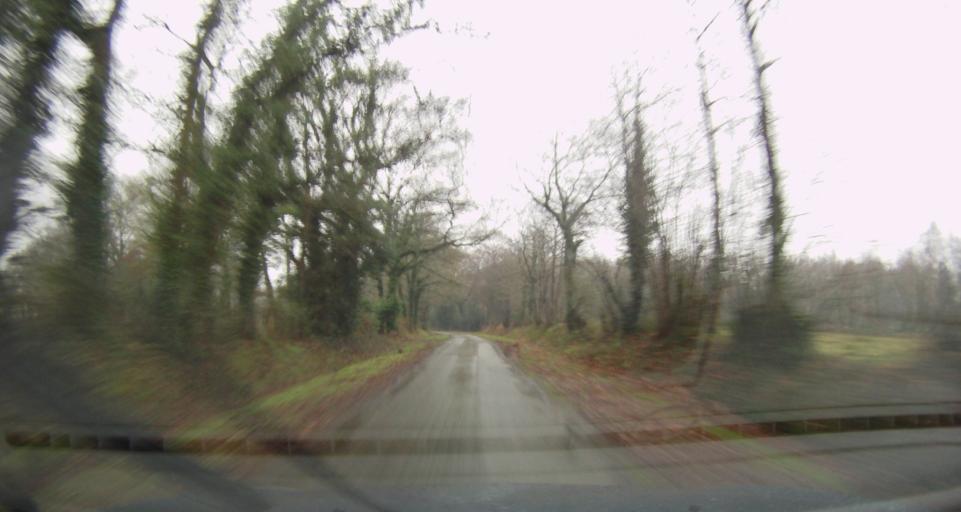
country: FR
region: Brittany
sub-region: Departement d'Ille-et-Vilaine
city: Orgeres
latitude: 47.9814
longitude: -1.6607
